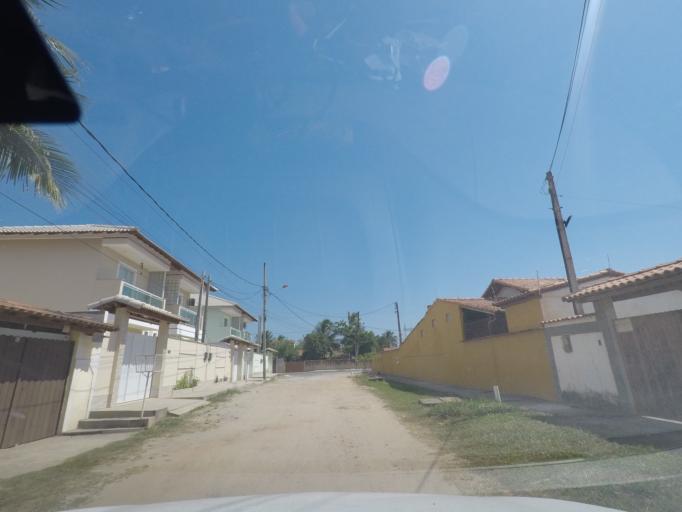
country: BR
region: Rio de Janeiro
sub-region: Marica
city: Marica
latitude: -22.9562
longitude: -42.9629
